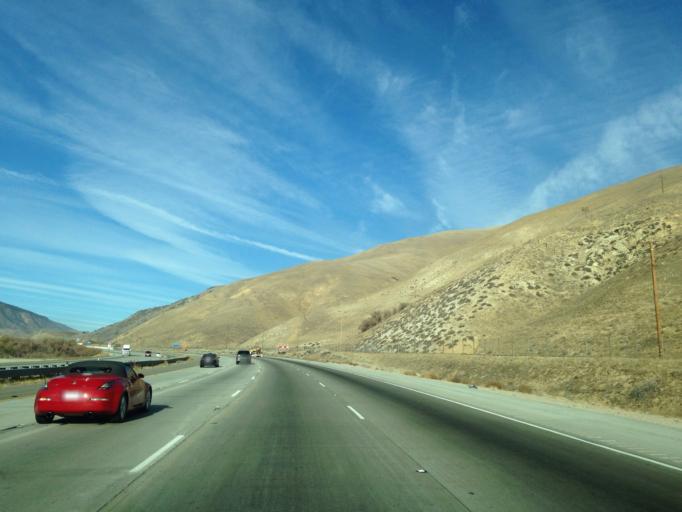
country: US
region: California
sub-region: Kern County
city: Lebec
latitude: 34.7921
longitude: -118.8346
